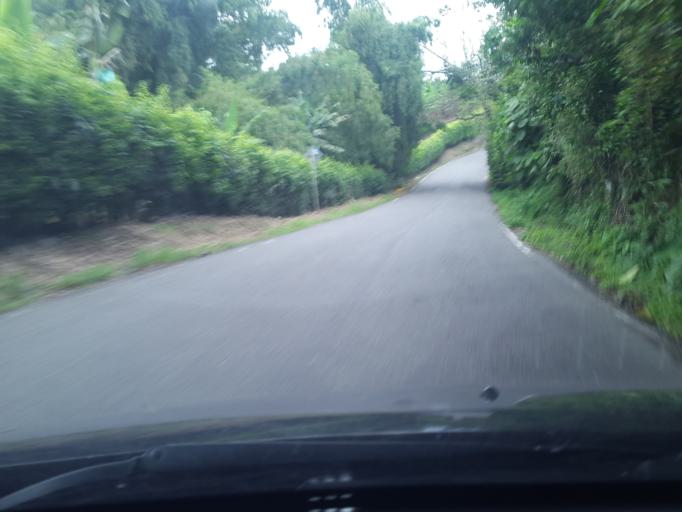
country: CO
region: Quindio
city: La Tebaida
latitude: 4.4853
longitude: -75.8025
